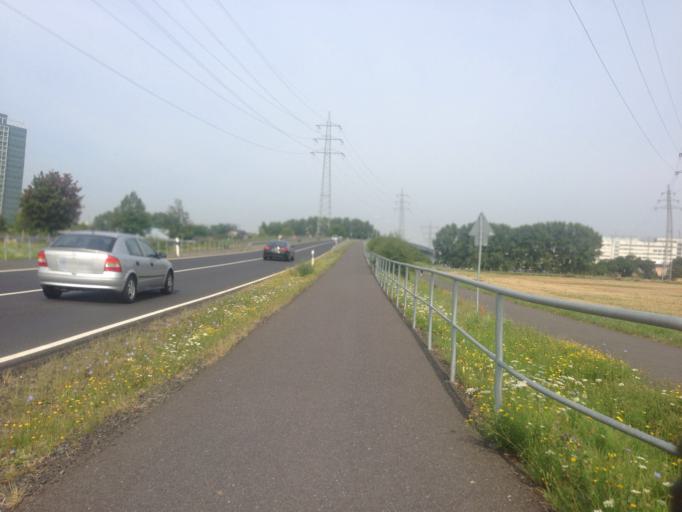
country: DE
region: Hesse
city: Kelsterbach
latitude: 50.0928
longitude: 8.5501
